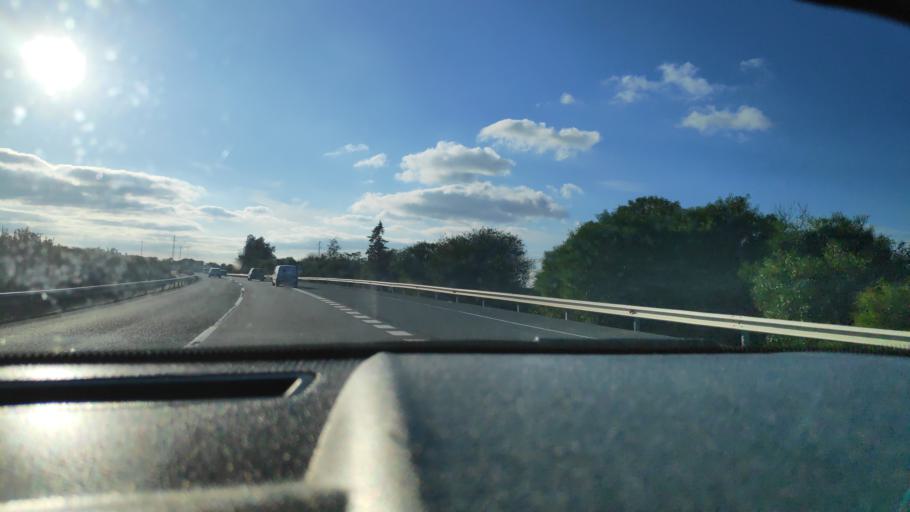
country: ES
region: Andalusia
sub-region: Provincia de Sevilla
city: Carmona
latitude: 37.4880
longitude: -5.6443
